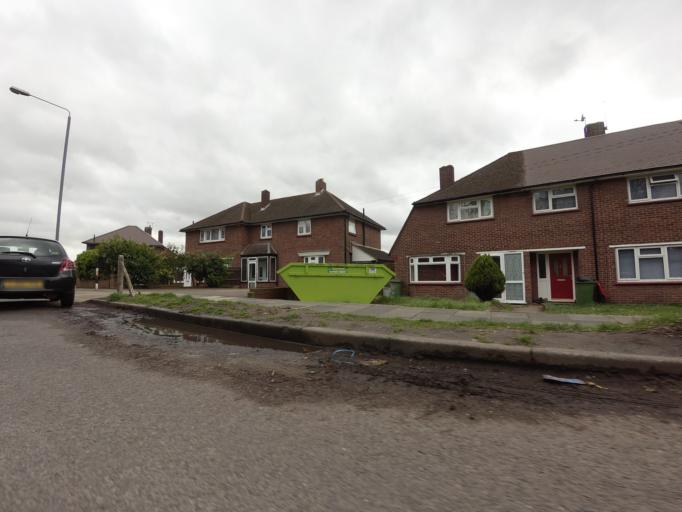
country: GB
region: England
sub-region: Greater London
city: Orpington
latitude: 51.3883
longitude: 0.1224
